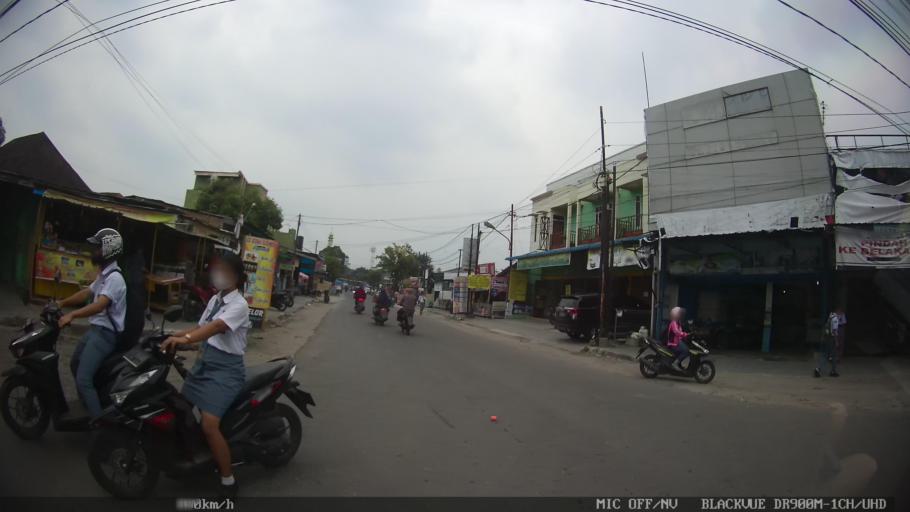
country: ID
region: North Sumatra
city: Medan
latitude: 3.5646
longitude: 98.7020
